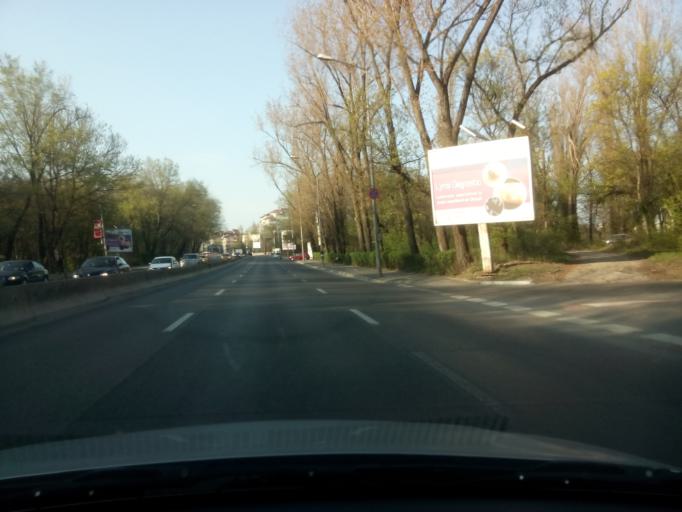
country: RO
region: Bucuresti
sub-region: Municipiul Bucuresti
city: Bucharest
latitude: 44.4876
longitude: 26.0781
